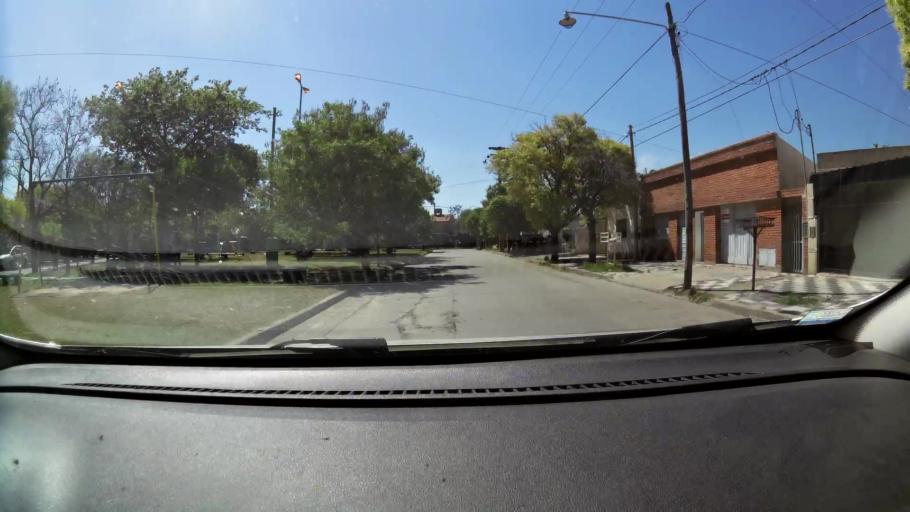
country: AR
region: Cordoba
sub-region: Departamento de Capital
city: Cordoba
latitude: -31.3768
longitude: -64.1545
